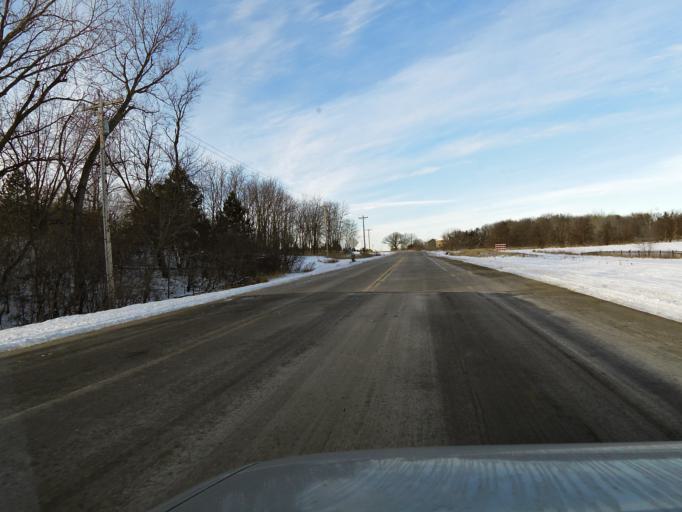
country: US
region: Minnesota
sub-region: Scott County
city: Prior Lake
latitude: 44.7657
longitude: -93.4227
